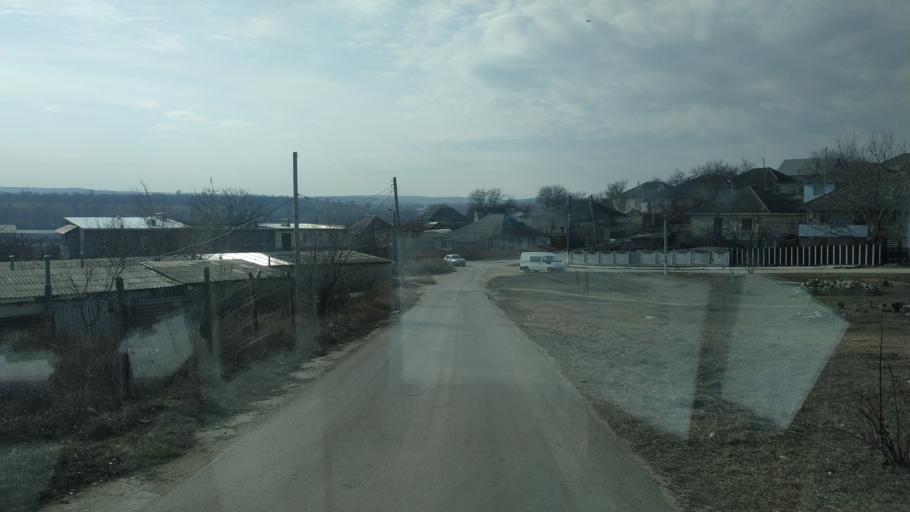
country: MD
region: Chisinau
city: Singera
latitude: 46.9275
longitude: 29.0664
